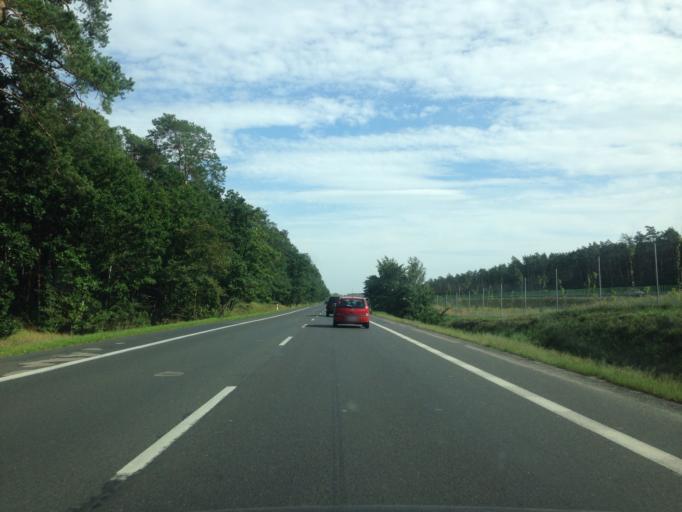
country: PL
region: Kujawsko-Pomorskie
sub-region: Powiat aleksandrowski
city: Aleksandrow Kujawski
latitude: 52.8846
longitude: 18.7381
